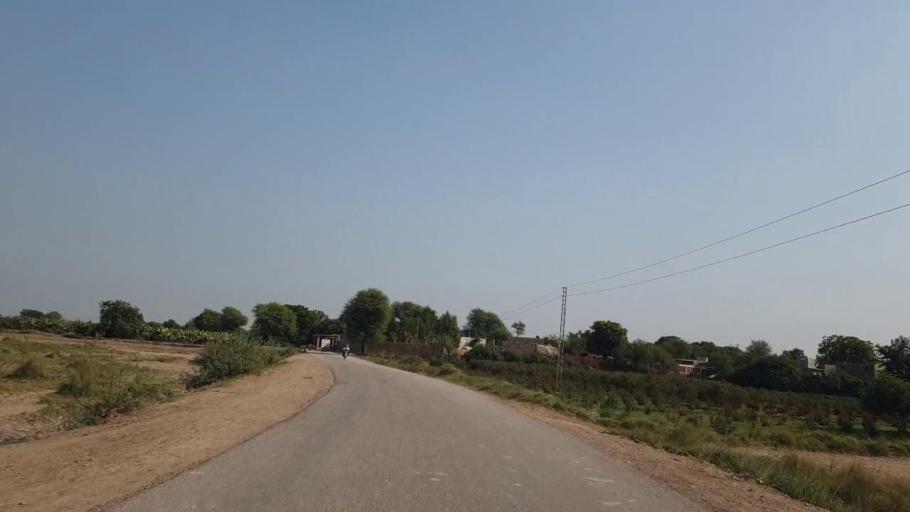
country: PK
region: Sindh
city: Matiari
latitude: 25.5011
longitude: 68.4427
